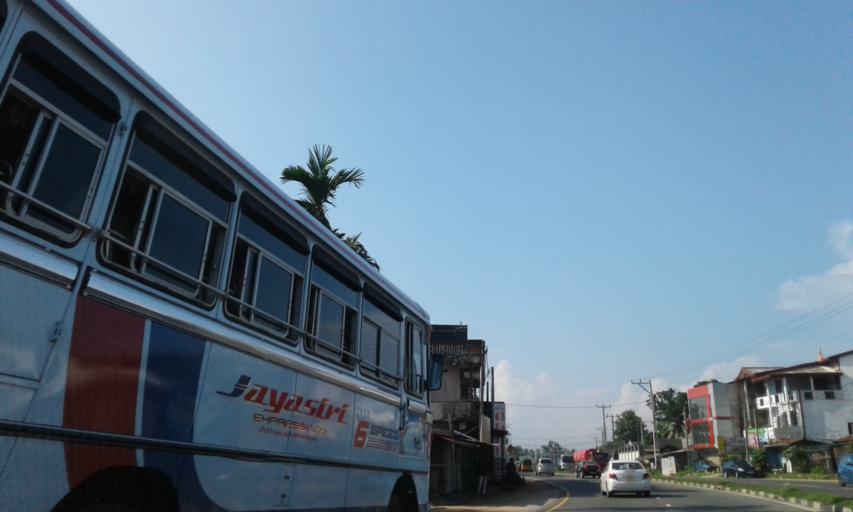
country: LK
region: Western
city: Welisara
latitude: 7.0137
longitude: 79.9675
